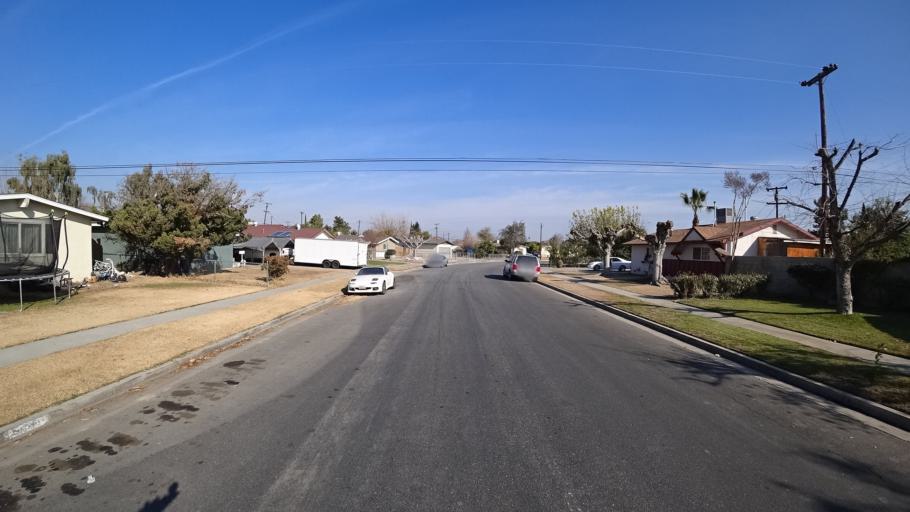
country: US
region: California
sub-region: Kern County
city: Bakersfield
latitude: 35.3235
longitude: -119.0184
